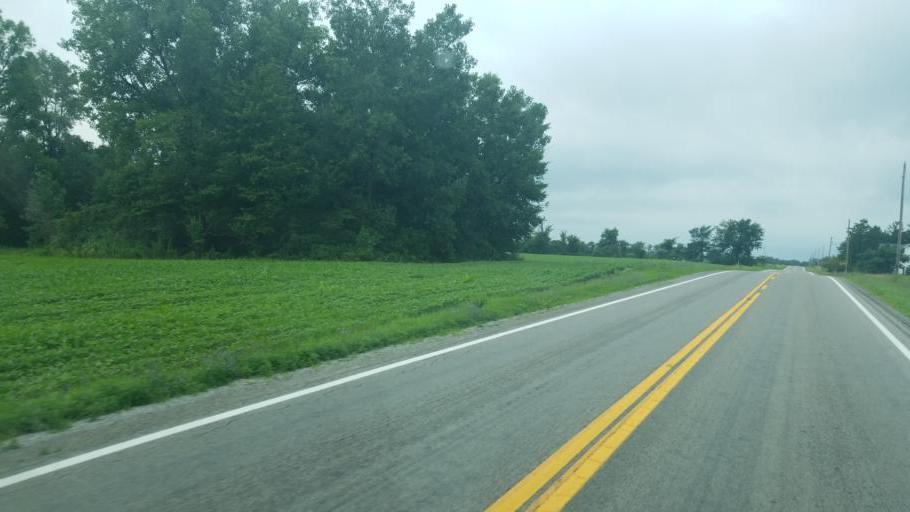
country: US
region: Ohio
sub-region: Logan County
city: Northwood
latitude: 40.5935
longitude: -83.7656
